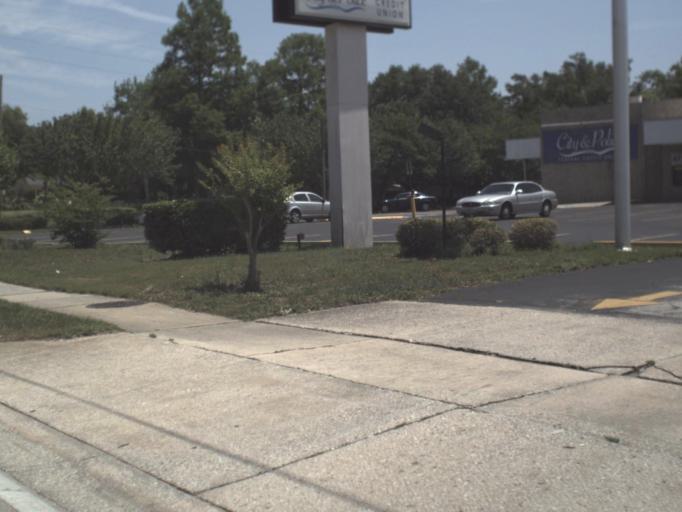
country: US
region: Florida
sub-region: Duval County
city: Jacksonville
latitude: 30.2941
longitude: -81.6075
